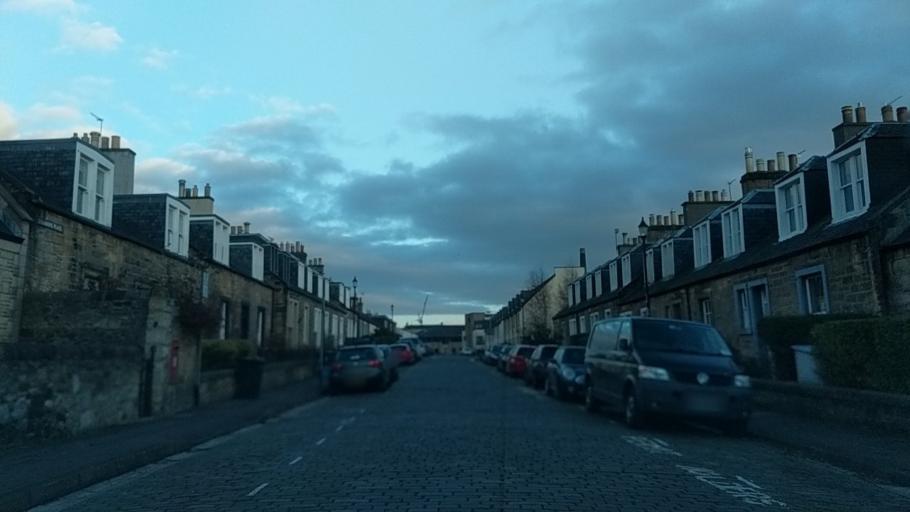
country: GB
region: Scotland
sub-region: Edinburgh
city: Edinburgh
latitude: 55.9450
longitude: -3.2272
